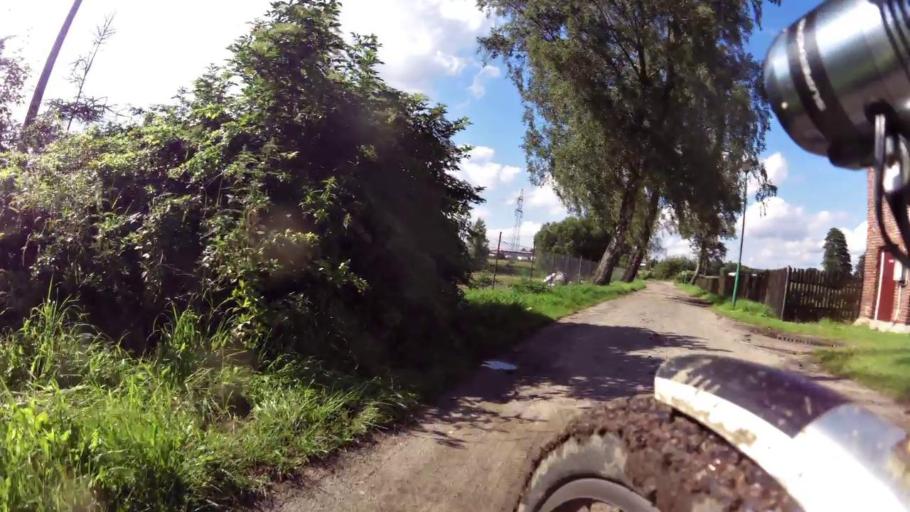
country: PL
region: West Pomeranian Voivodeship
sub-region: Powiat swidwinski
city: Swidwin
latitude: 53.7580
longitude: 15.7518
